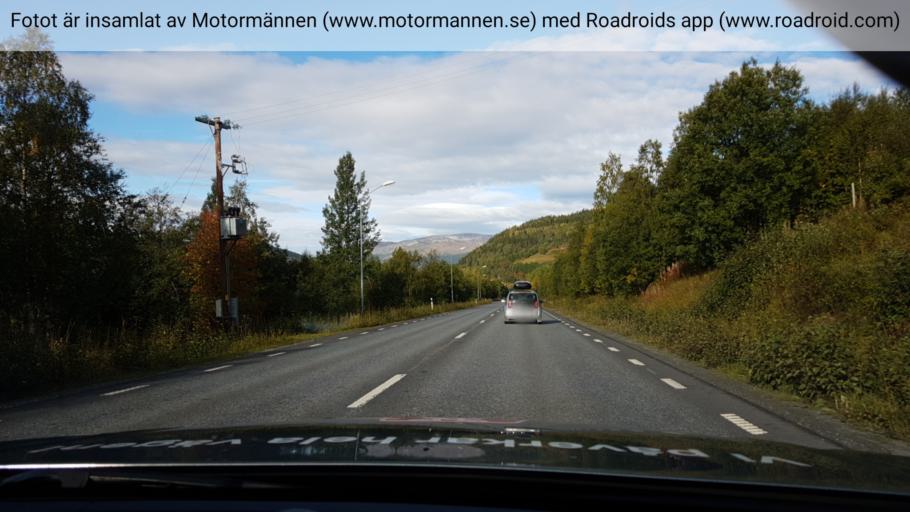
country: SE
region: Jaemtland
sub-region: Are Kommun
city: Are
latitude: 63.3810
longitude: 13.1438
